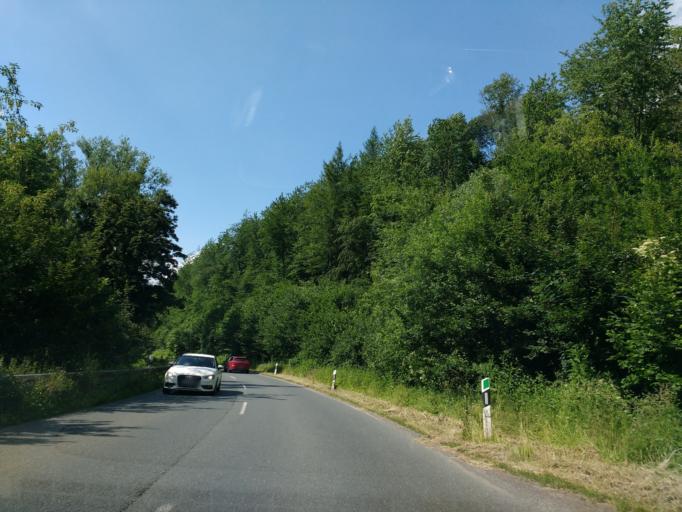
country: DE
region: North Rhine-Westphalia
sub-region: Regierungsbezirk Detmold
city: Dorentrup
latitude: 52.1206
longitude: 8.9485
